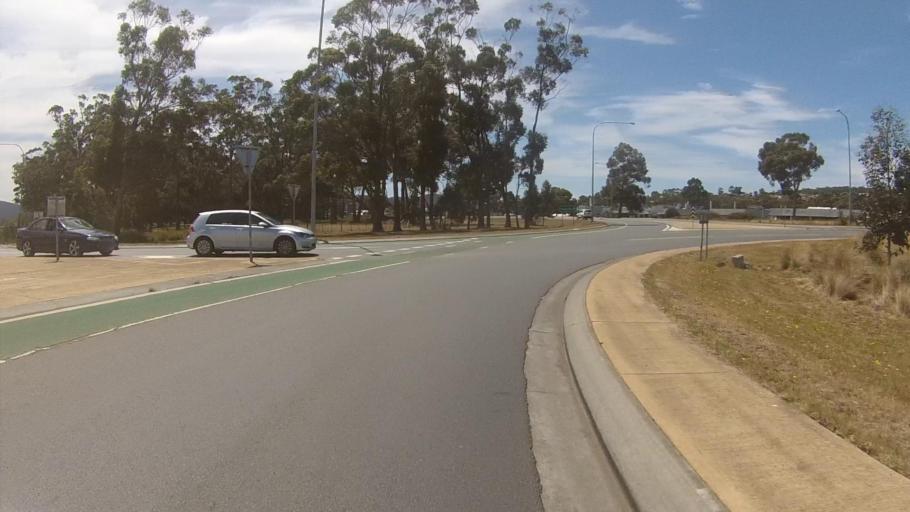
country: AU
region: Tasmania
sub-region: Kingborough
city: Kingston
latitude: -42.9870
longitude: 147.2891
